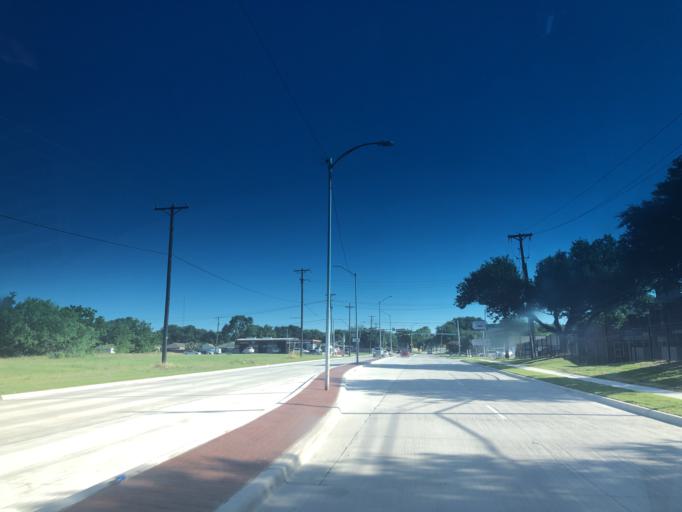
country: US
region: Texas
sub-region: Dallas County
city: Grand Prairie
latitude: 32.7121
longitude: -97.0153
